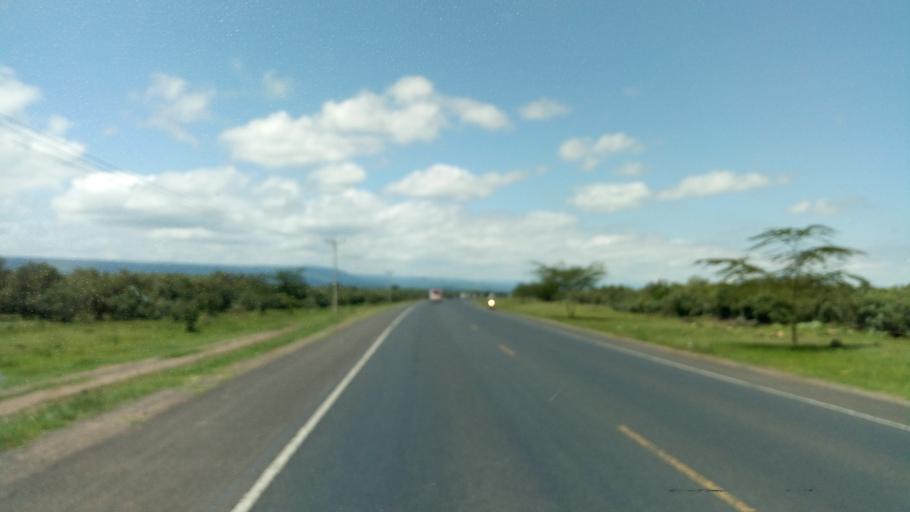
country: KE
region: Nakuru
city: Naivasha
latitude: -0.5460
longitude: 36.3433
